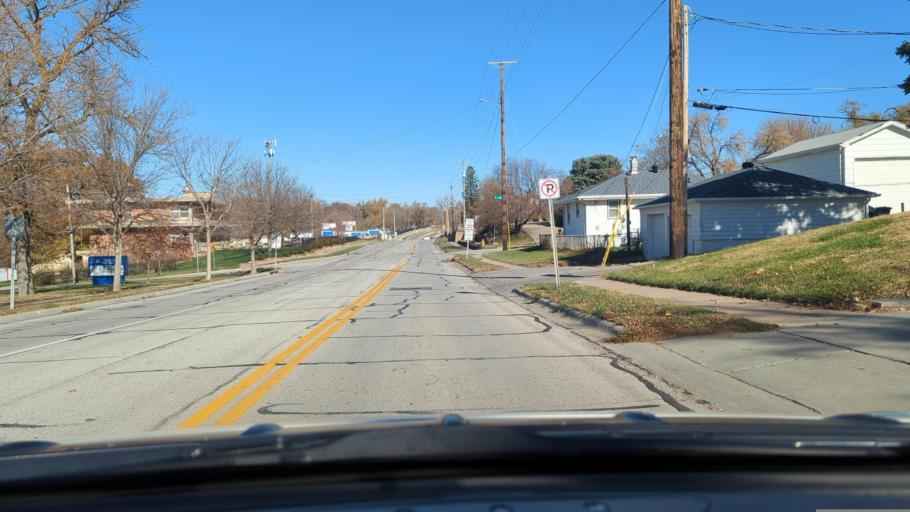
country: US
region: Nebraska
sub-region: Sarpy County
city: La Vista
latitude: 41.2020
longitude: -95.9770
